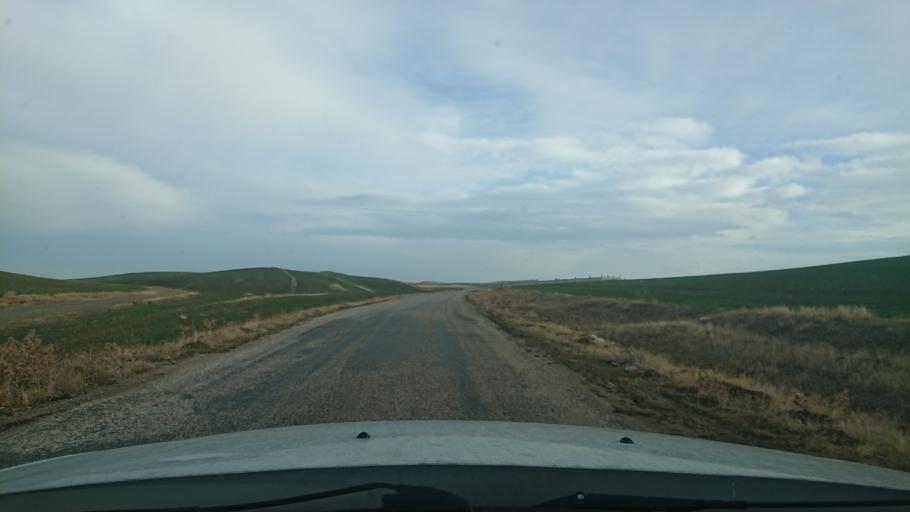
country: TR
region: Aksaray
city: Acipinar
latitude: 38.6344
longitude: 33.8021
